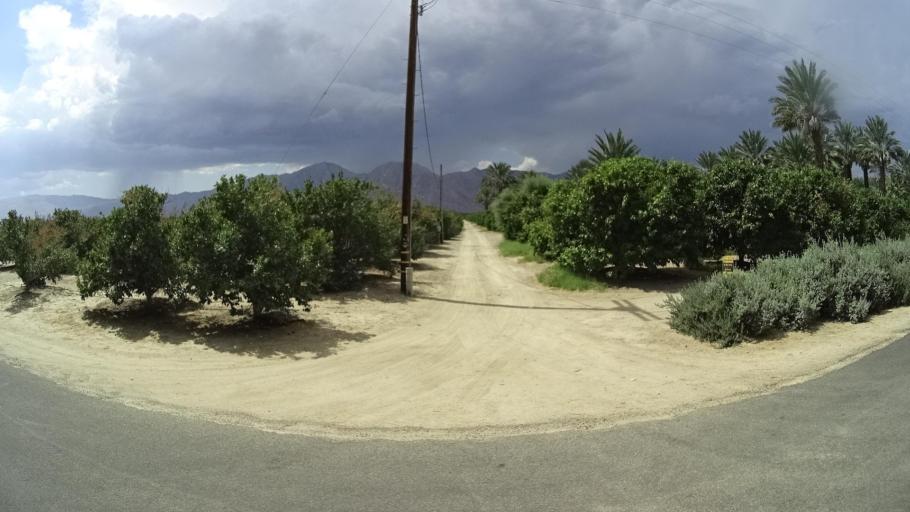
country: US
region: California
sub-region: San Diego County
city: Borrego Springs
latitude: 33.3056
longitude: -116.3496
